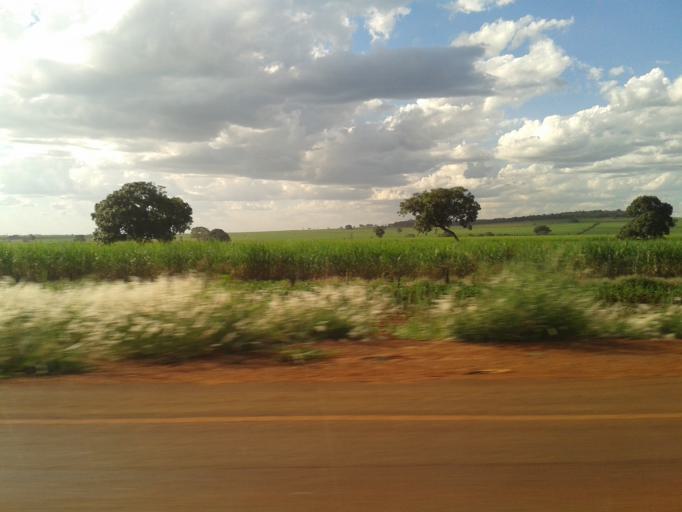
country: BR
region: Minas Gerais
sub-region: Santa Vitoria
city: Santa Vitoria
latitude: -18.6937
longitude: -49.9189
